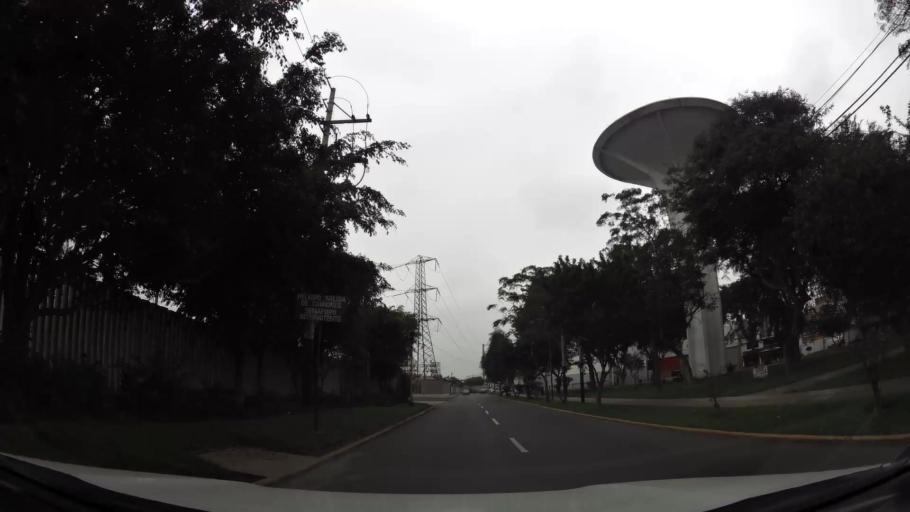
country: PE
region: Lima
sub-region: Lima
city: Surco
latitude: -12.1132
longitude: -76.9944
